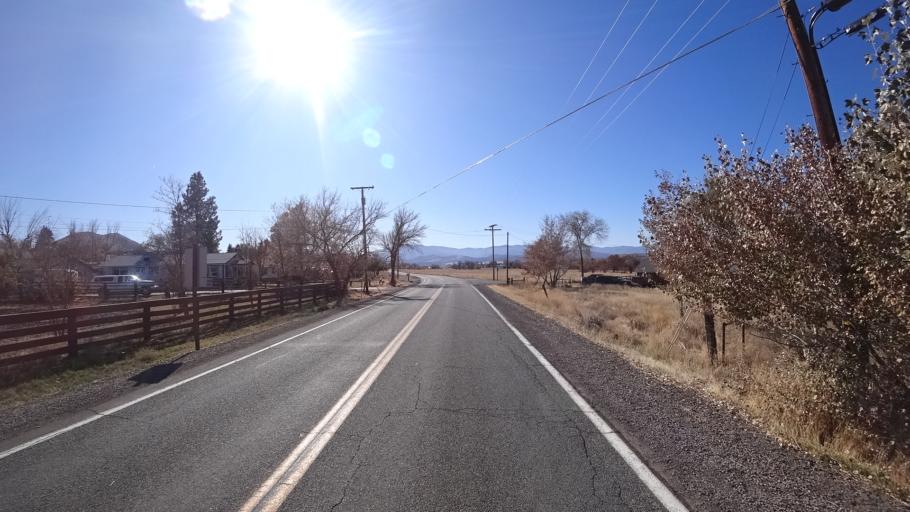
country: US
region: California
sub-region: Siskiyou County
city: Montague
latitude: 41.7349
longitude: -122.5188
